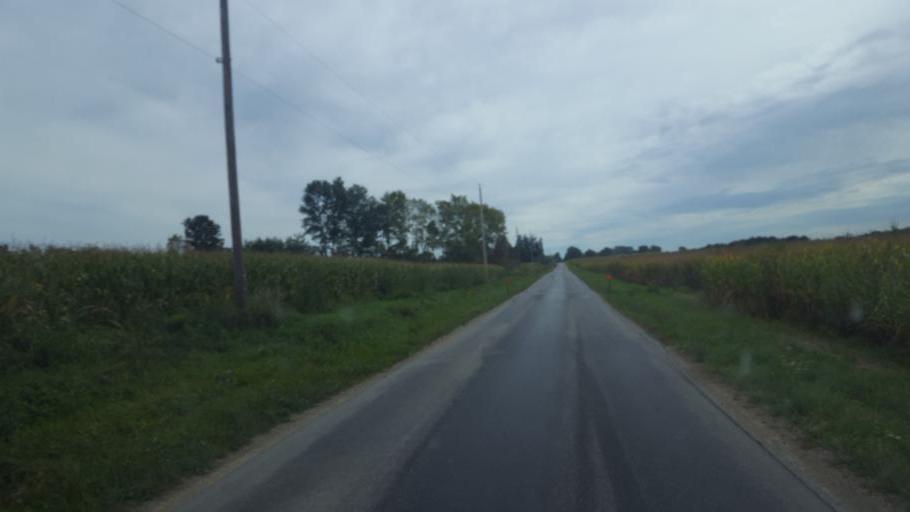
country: US
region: Ohio
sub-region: Knox County
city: Centerburg
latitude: 40.3211
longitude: -82.7162
